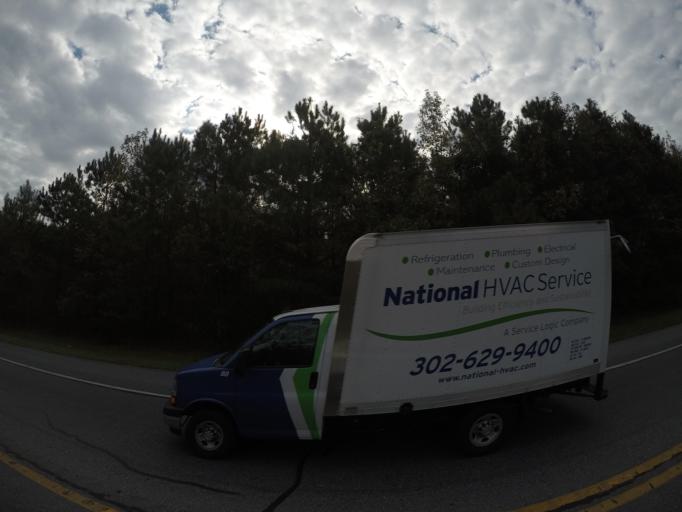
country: US
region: Delaware
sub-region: Sussex County
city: Milton
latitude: 38.7183
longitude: -75.3068
